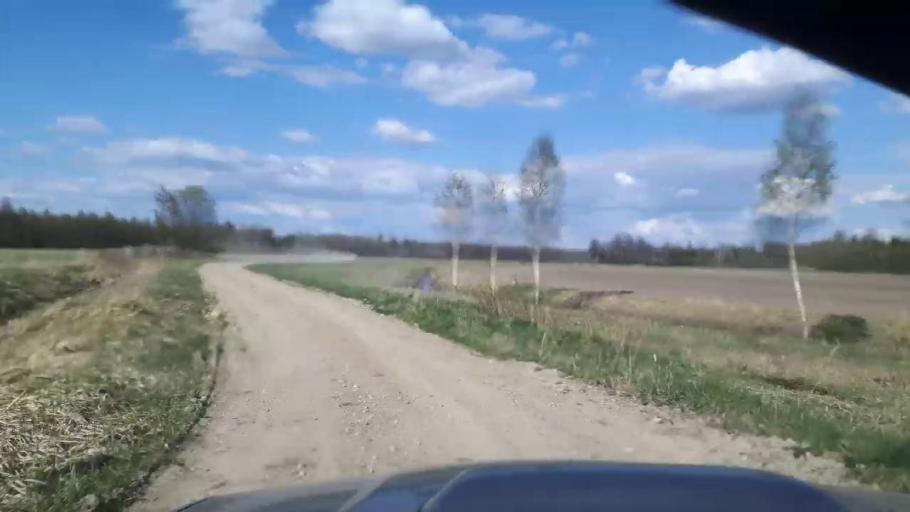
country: EE
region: Paernumaa
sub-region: Tootsi vald
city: Tootsi
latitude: 58.4390
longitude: 24.8741
